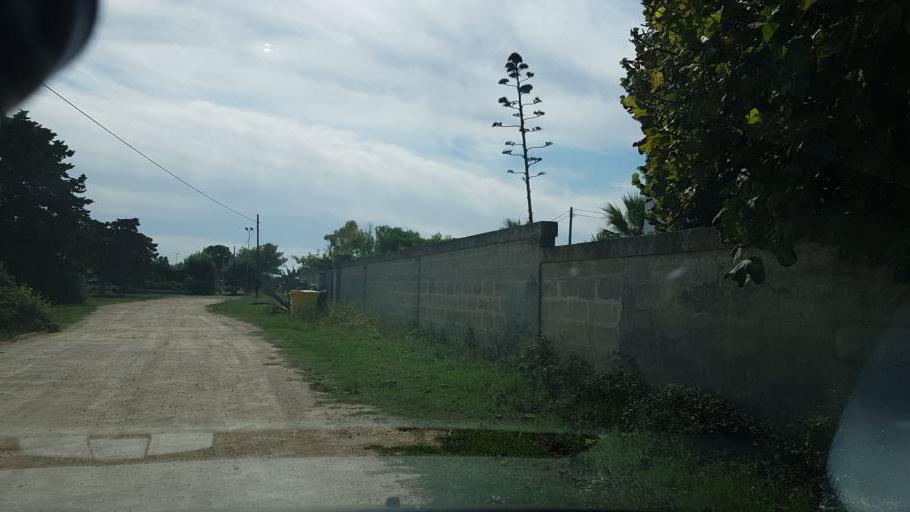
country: IT
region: Apulia
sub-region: Provincia di Lecce
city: Borgagne
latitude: 40.2295
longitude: 18.4415
